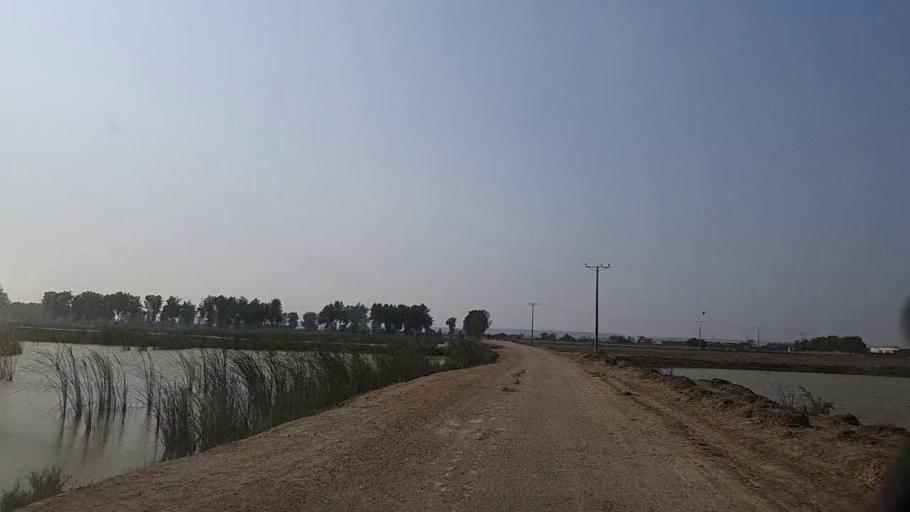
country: PK
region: Sindh
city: Thatta
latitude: 24.6062
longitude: 67.8952
